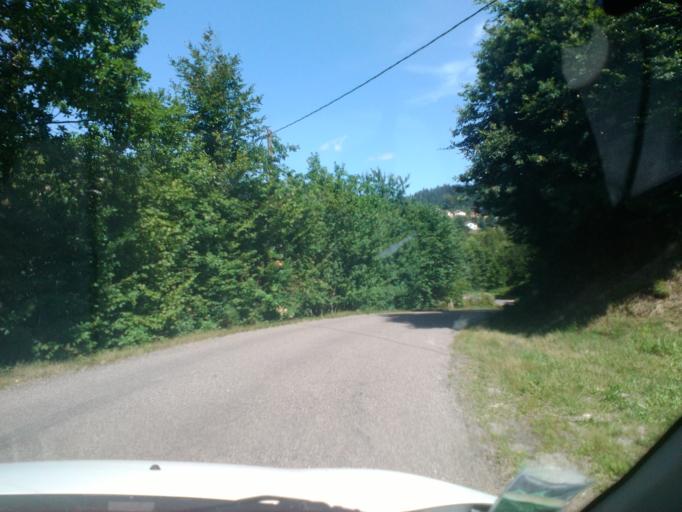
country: FR
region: Lorraine
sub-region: Departement des Vosges
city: Le Tholy
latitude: 48.0776
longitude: 6.7434
